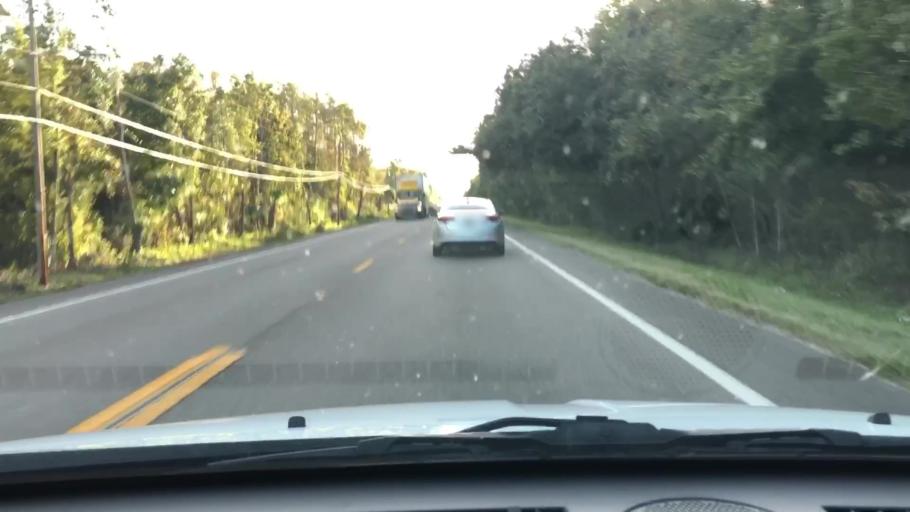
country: US
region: Florida
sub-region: Osceola County
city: Campbell
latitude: 28.2594
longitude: -81.5027
